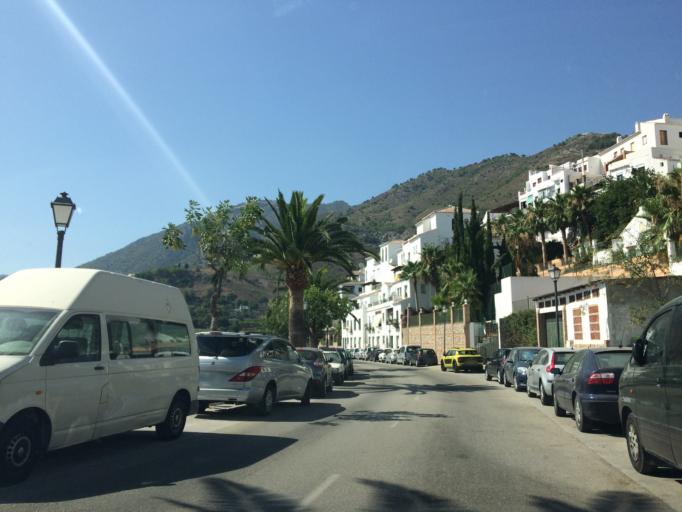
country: ES
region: Andalusia
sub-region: Provincia de Malaga
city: Frigiliana
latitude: 36.7918
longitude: -3.8991
